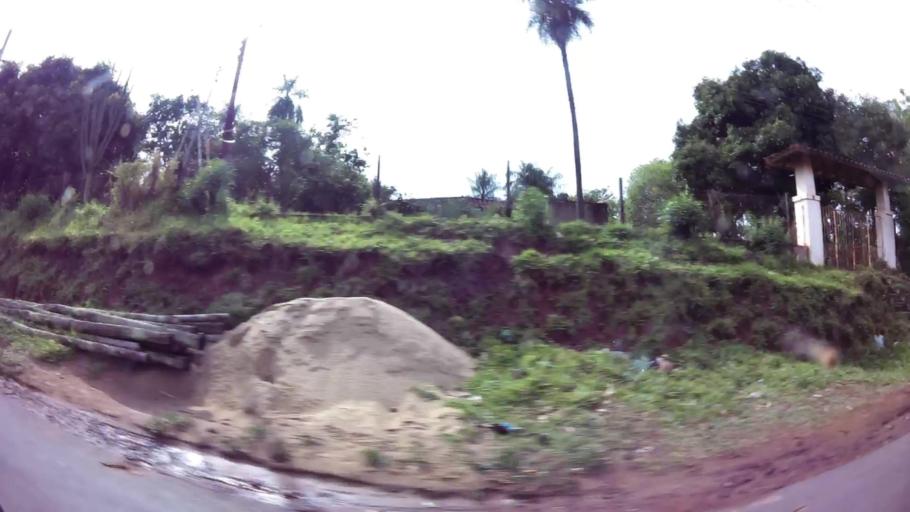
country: PY
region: Central
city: Limpio
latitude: -25.1527
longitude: -57.4619
